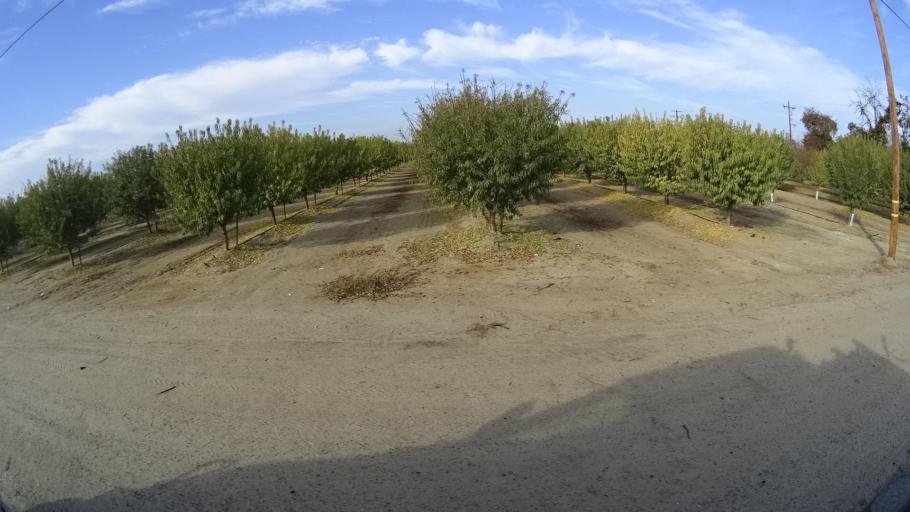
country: US
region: California
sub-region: Kern County
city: Delano
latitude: 35.7570
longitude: -119.2053
